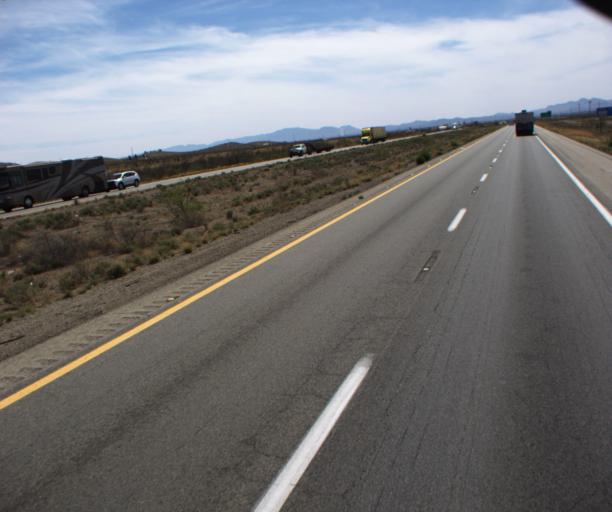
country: US
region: Arizona
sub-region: Cochise County
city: Willcox
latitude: 32.3214
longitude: -109.7799
